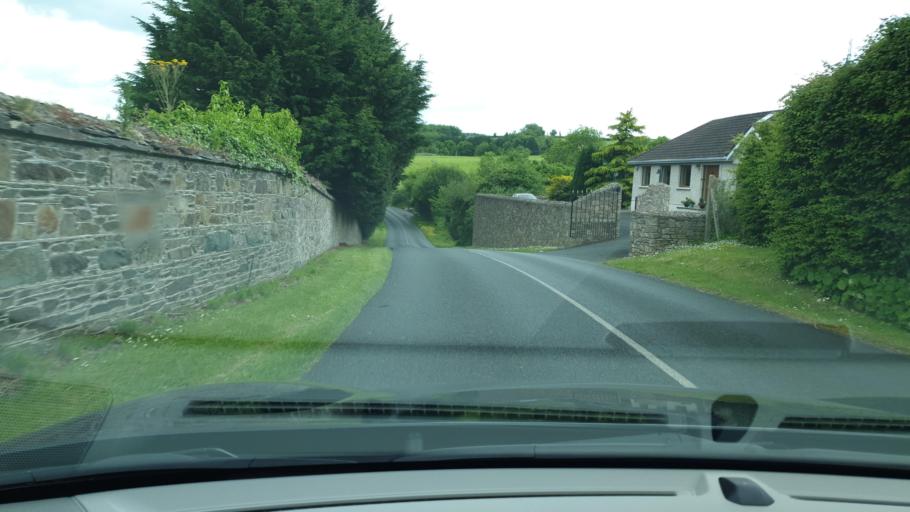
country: IE
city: Kilquade
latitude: 53.0942
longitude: -6.0849
